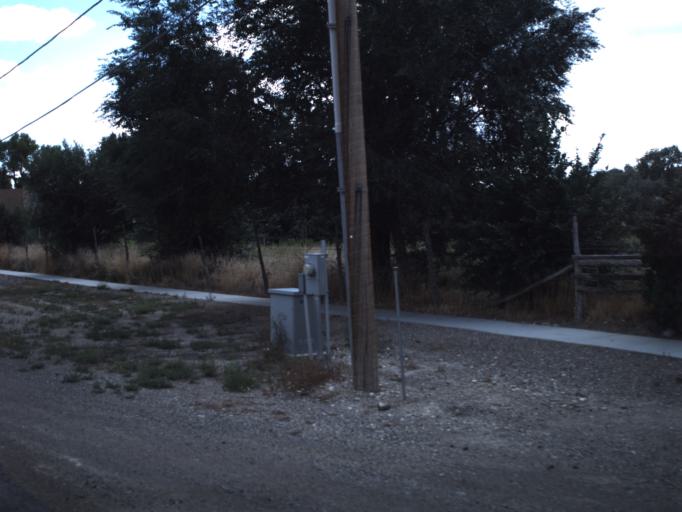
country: US
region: Utah
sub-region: Sanpete County
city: Centerfield
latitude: 39.1171
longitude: -111.7108
